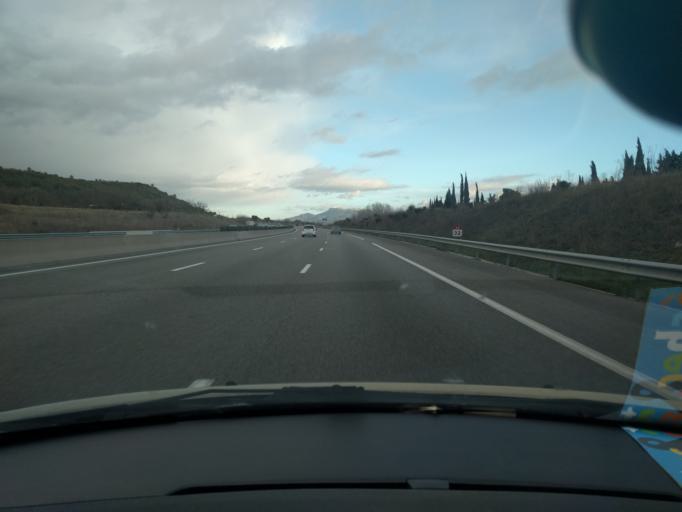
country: FR
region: Provence-Alpes-Cote d'Azur
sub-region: Departement des Bouches-du-Rhone
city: Chateauneuf-le-Rouge
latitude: 43.4799
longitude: 5.5785
